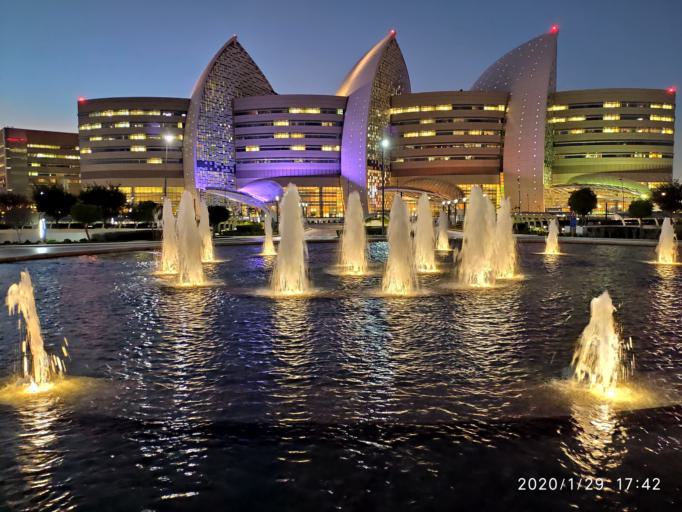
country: QA
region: Baladiyat ar Rayyan
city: Ar Rayyan
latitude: 25.3209
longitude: 51.4464
